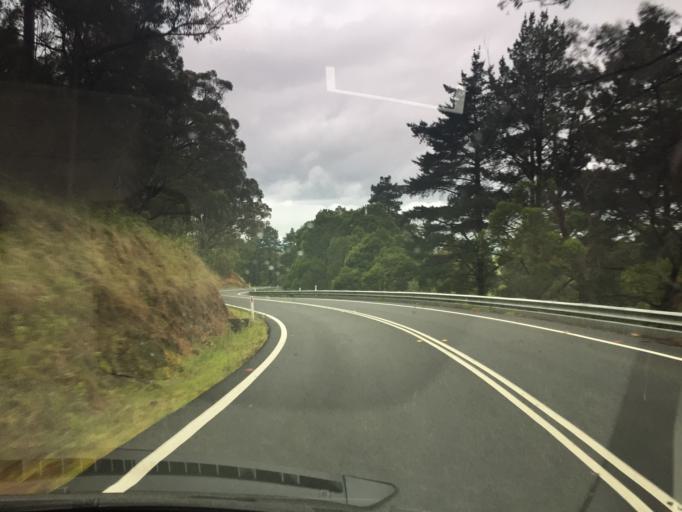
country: AU
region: New South Wales
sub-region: Bega Valley
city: Bega
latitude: -36.6116
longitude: 149.4875
